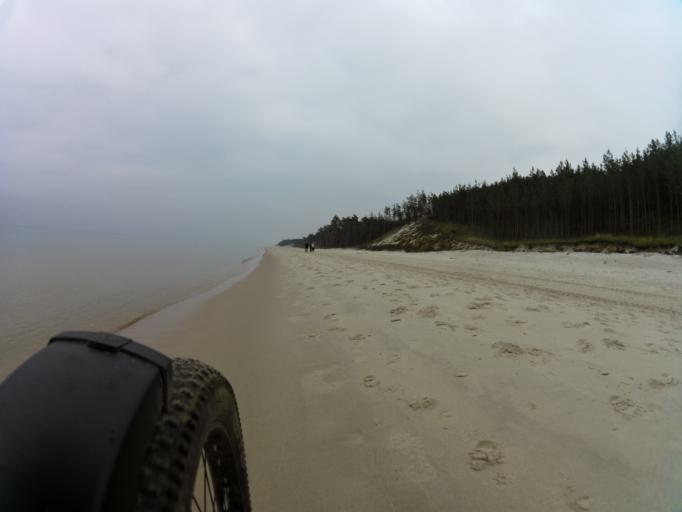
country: PL
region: Pomeranian Voivodeship
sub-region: Powiat pucki
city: Krokowa
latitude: 54.8321
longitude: 18.1274
